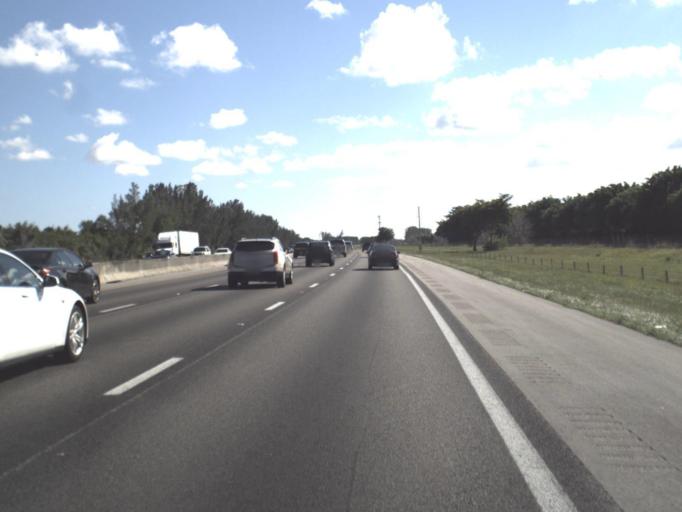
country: US
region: Florida
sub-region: Palm Beach County
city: Villages of Oriole
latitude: 26.4376
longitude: -80.1741
